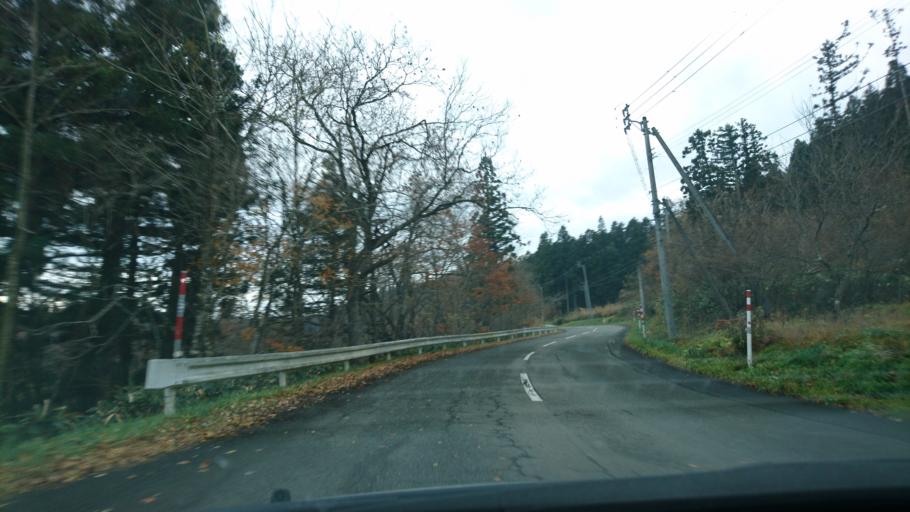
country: JP
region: Iwate
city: Ichinoseki
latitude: 38.9397
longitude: 140.9222
